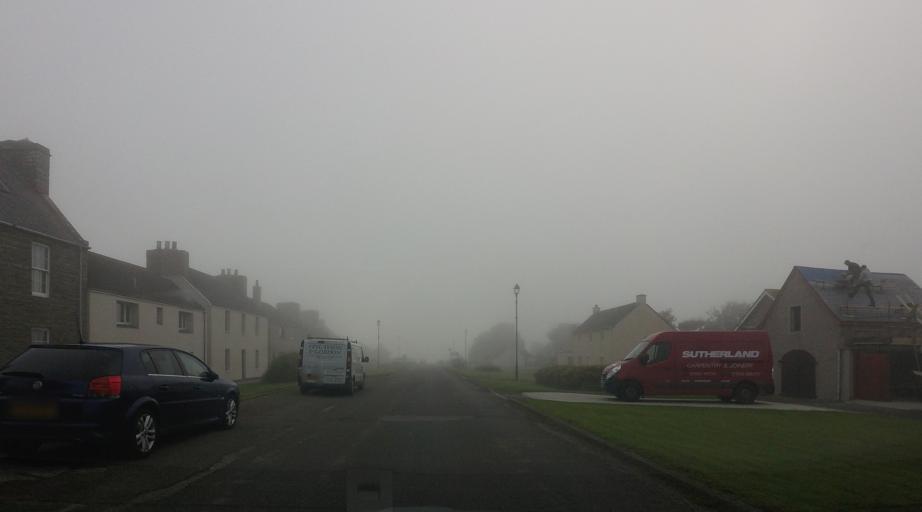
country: GB
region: Scotland
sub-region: Highland
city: Wick
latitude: 58.3003
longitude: -3.2845
